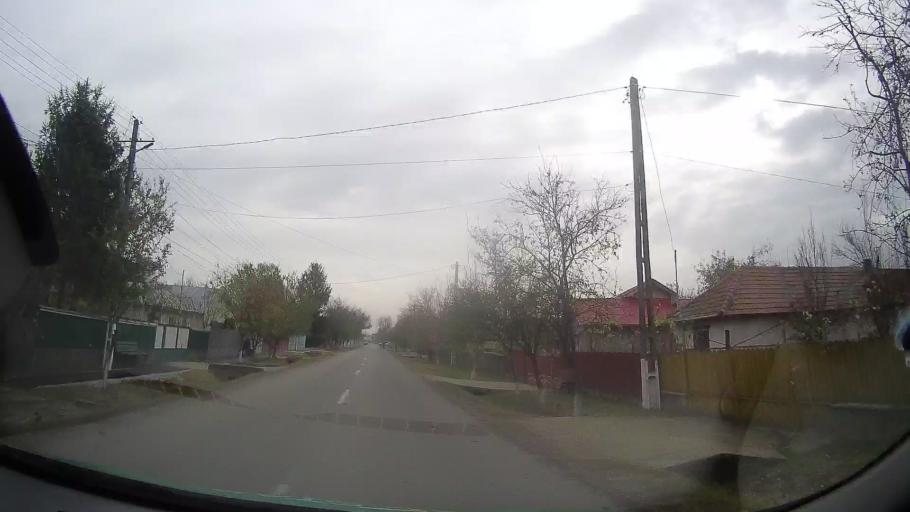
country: RO
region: Prahova
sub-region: Comuna Dumbrava
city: Dumbrava
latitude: 44.8765
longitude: 26.1852
